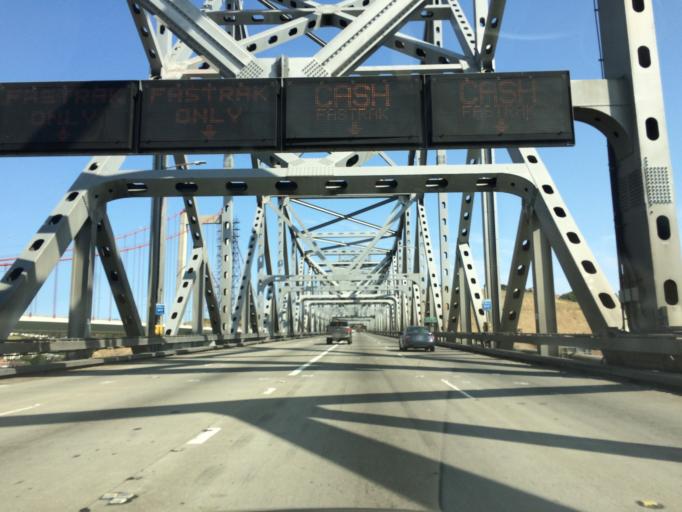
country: US
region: California
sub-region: Contra Costa County
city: Crockett
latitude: 38.0609
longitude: -122.2252
